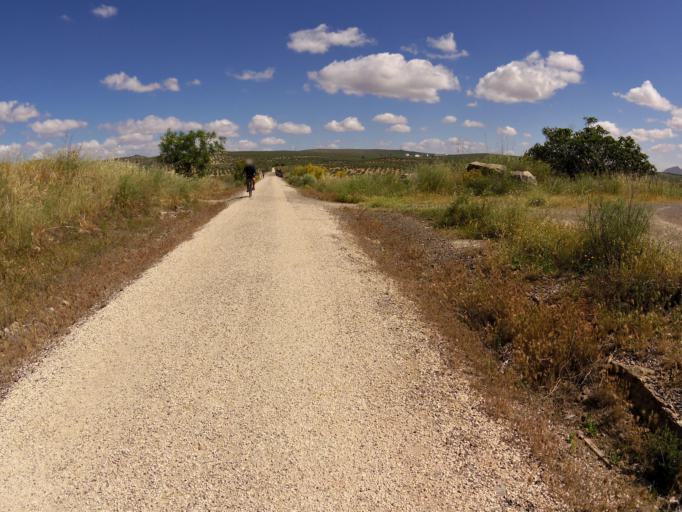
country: ES
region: Andalusia
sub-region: Provincia de Jaen
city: Alcaudete
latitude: 37.6353
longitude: -4.0824
